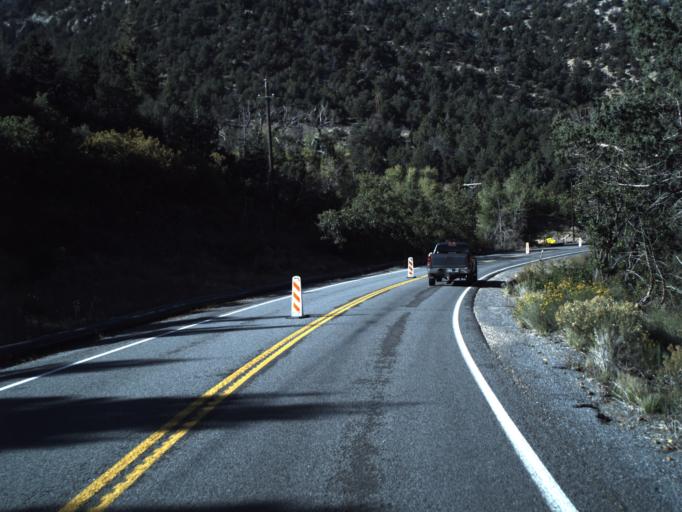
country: US
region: Utah
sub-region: Iron County
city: Parowan
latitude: 37.7623
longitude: -112.8506
